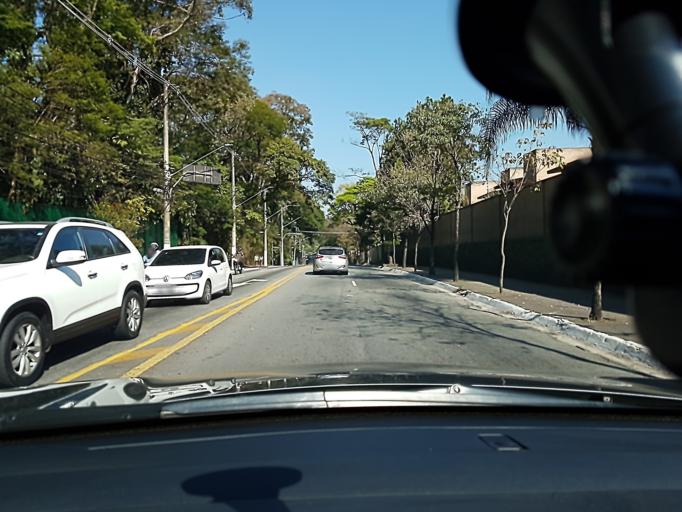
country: BR
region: Sao Paulo
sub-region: Taboao Da Serra
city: Taboao da Serra
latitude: -23.6046
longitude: -46.7124
